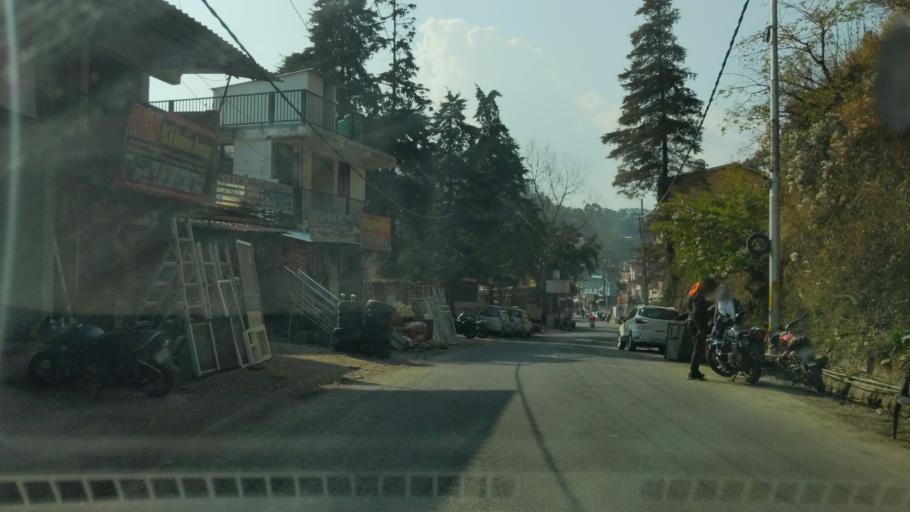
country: IN
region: Uttarakhand
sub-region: Naini Tal
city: Bhowali
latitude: 29.3834
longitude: 79.5239
